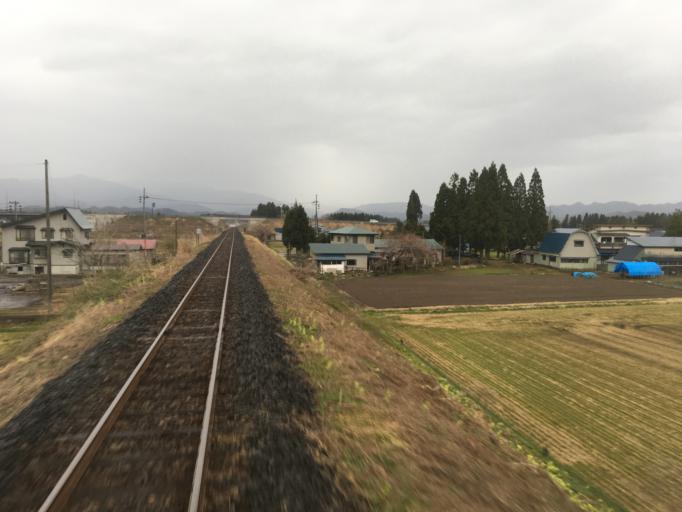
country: JP
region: Akita
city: Kakunodatemachi
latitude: 39.6107
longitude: 140.5779
